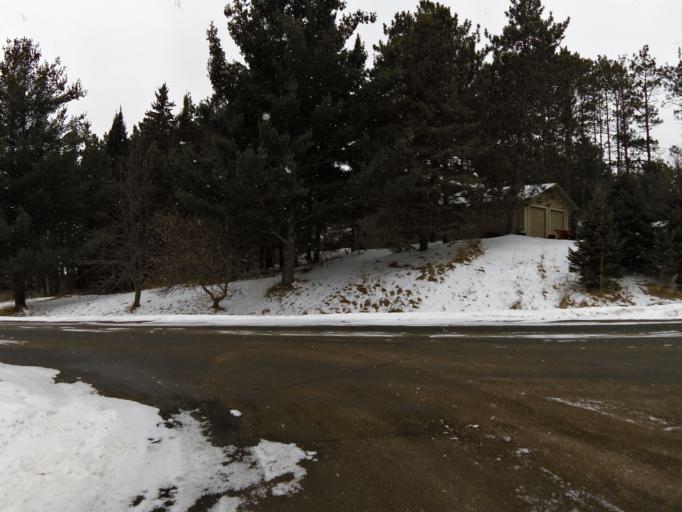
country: US
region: Minnesota
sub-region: Washington County
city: Lake Elmo
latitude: 44.9759
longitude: -92.8437
